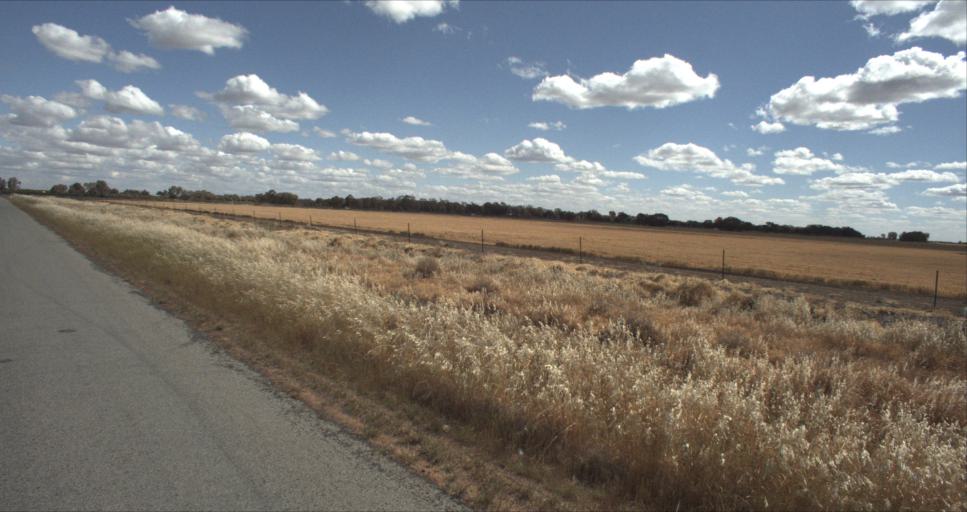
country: AU
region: New South Wales
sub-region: Leeton
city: Leeton
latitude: -34.5019
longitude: 146.2453
